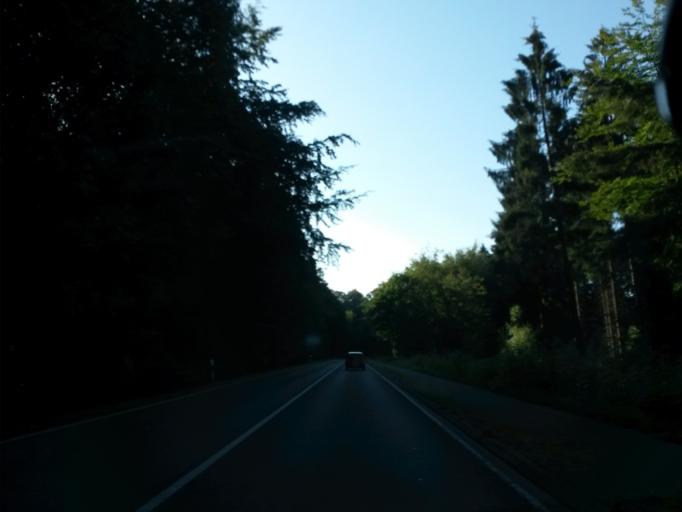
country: DE
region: North Rhine-Westphalia
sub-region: Regierungsbezirk Koln
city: Rosrath
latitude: 50.9348
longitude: 7.1713
